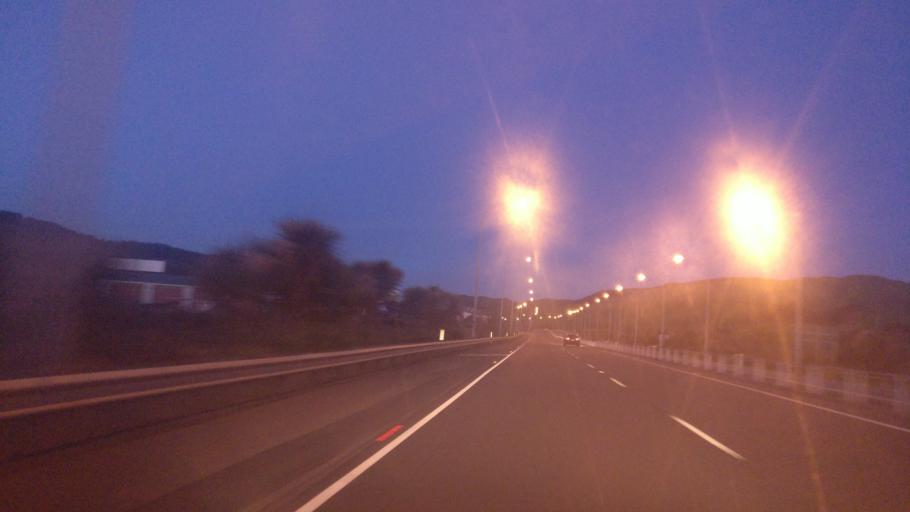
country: NZ
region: Wellington
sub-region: Porirua City
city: Porirua
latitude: -41.0814
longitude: 174.8706
